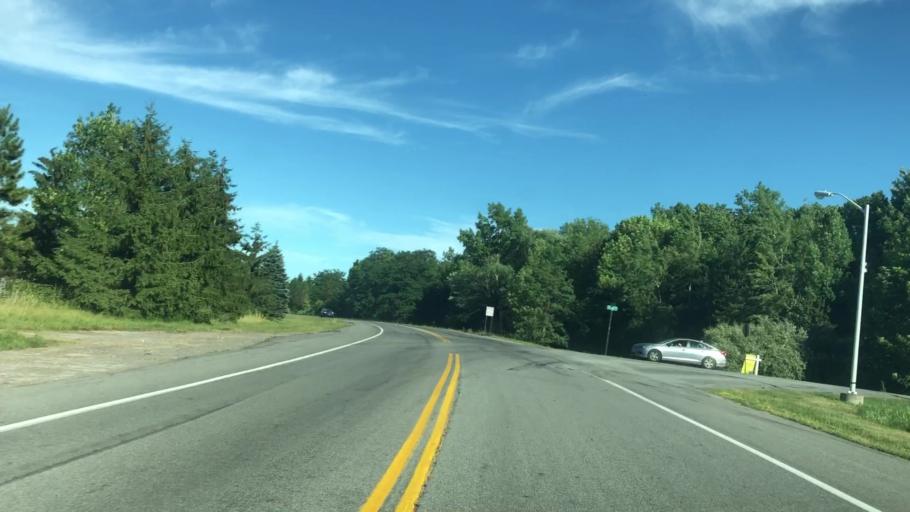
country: US
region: New York
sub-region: Wayne County
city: Macedon
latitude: 43.1244
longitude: -77.3376
